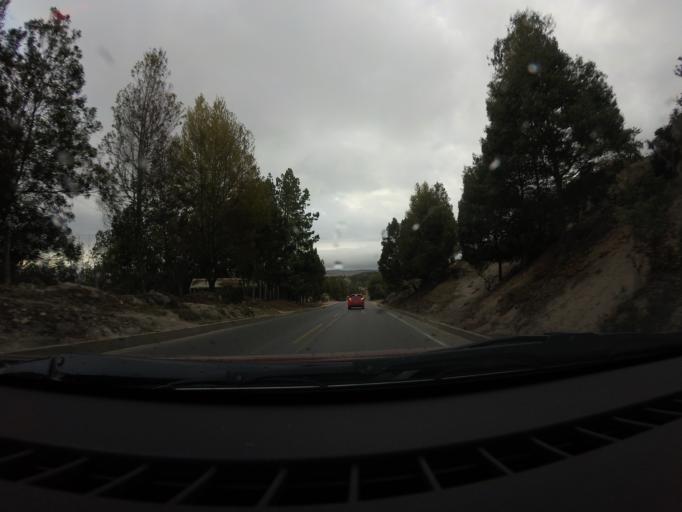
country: CO
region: Boyaca
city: Tunja
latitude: 5.5517
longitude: -73.4068
